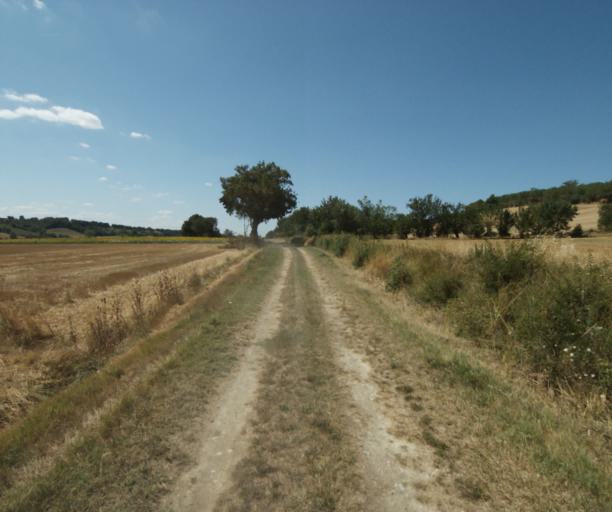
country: FR
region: Midi-Pyrenees
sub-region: Departement de la Haute-Garonne
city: Saint-Felix-Lauragais
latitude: 43.4965
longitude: 1.8747
